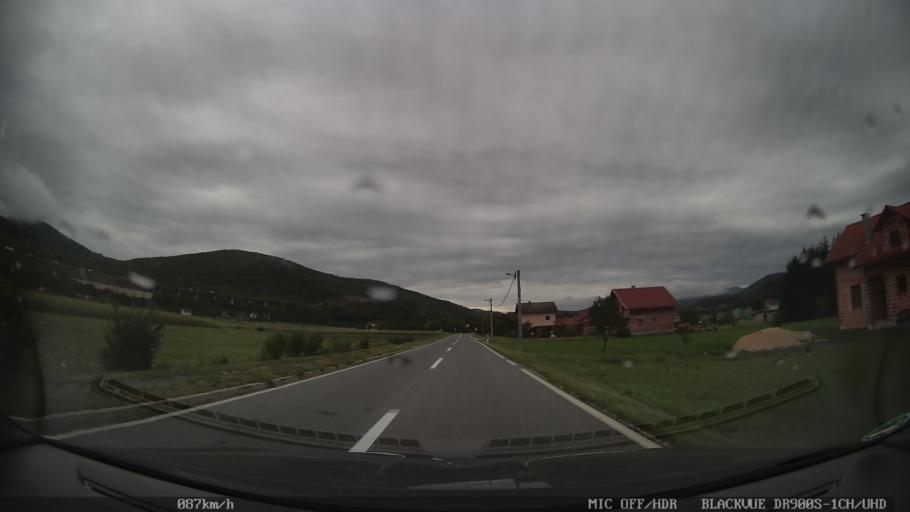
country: HR
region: Licko-Senjska
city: Otocac
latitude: 44.9088
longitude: 15.1677
